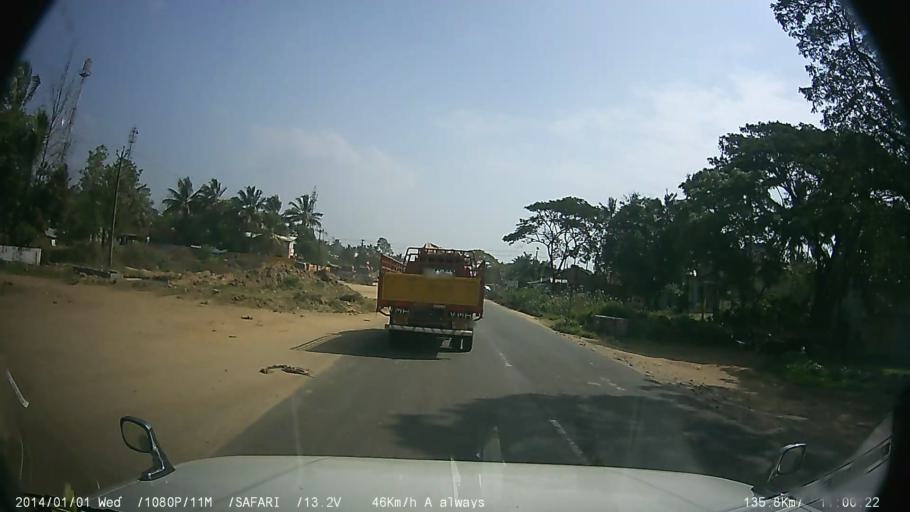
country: IN
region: Kerala
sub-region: Palakkad district
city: Palakkad
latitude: 10.7380
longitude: 76.6341
